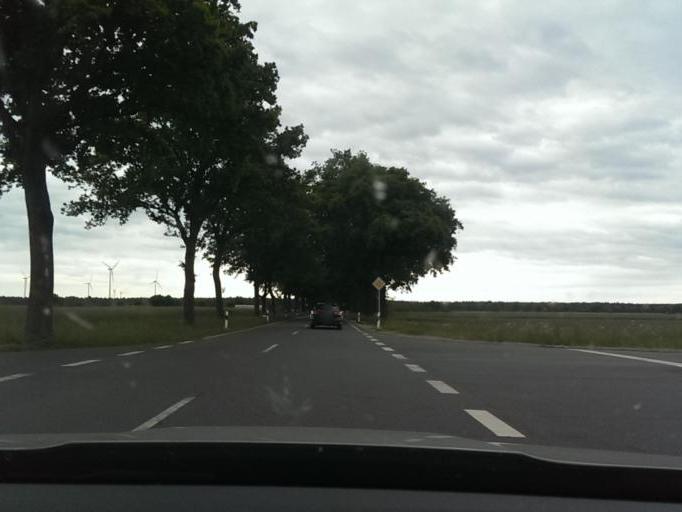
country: DE
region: Lower Saxony
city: Essel
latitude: 52.6651
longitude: 9.6629
